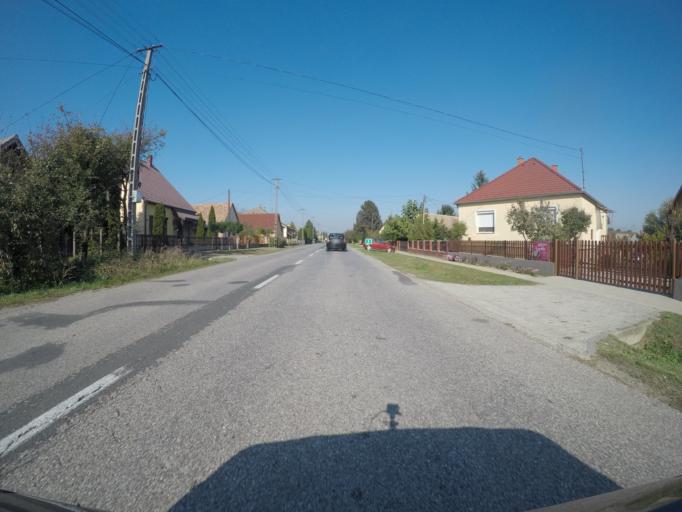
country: HU
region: Tolna
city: Szedres
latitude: 46.4783
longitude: 18.6836
